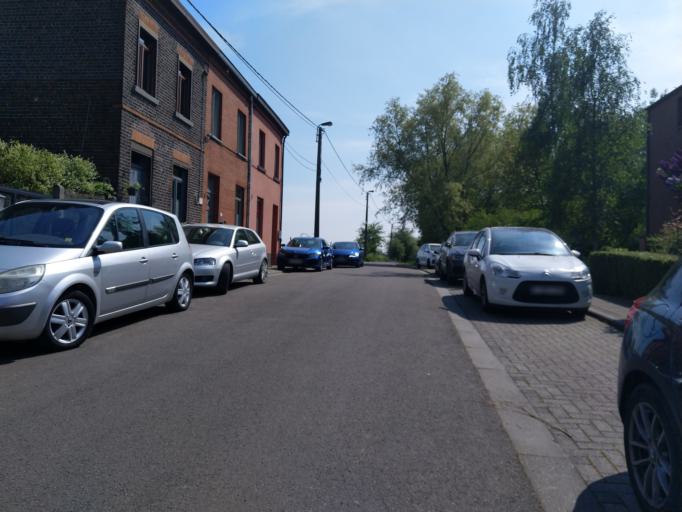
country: BE
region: Wallonia
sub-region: Province du Hainaut
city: Mons
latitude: 50.4670
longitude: 3.9671
